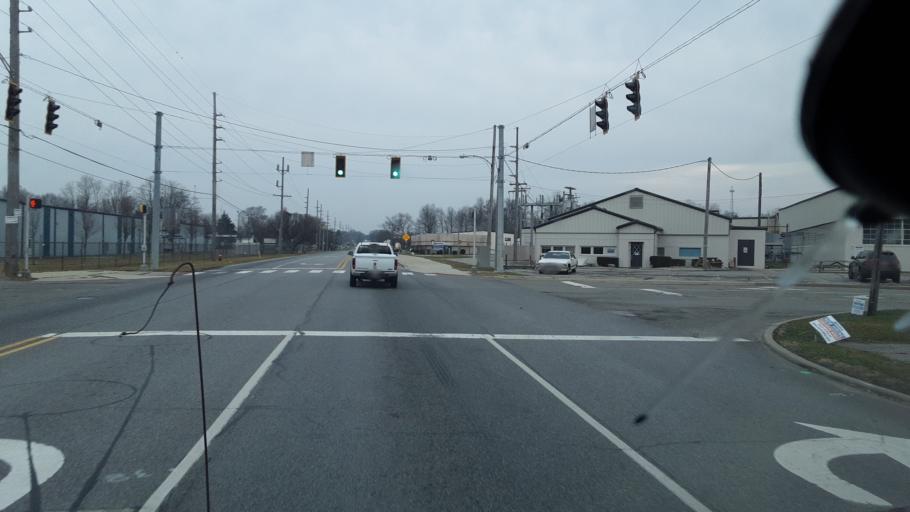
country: US
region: Indiana
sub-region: Elkhart County
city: Middlebury
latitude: 41.6813
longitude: -85.7037
